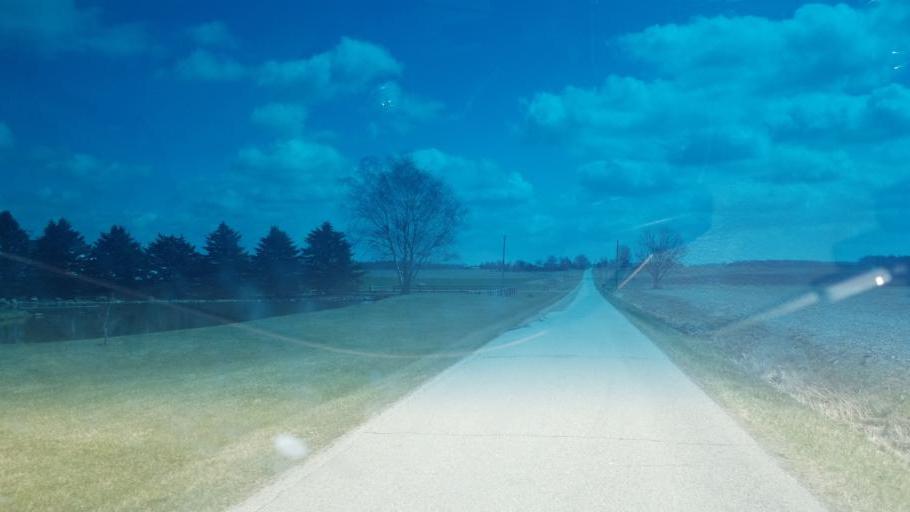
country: US
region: Ohio
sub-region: Crawford County
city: Bucyrus
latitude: 40.8485
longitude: -83.0497
